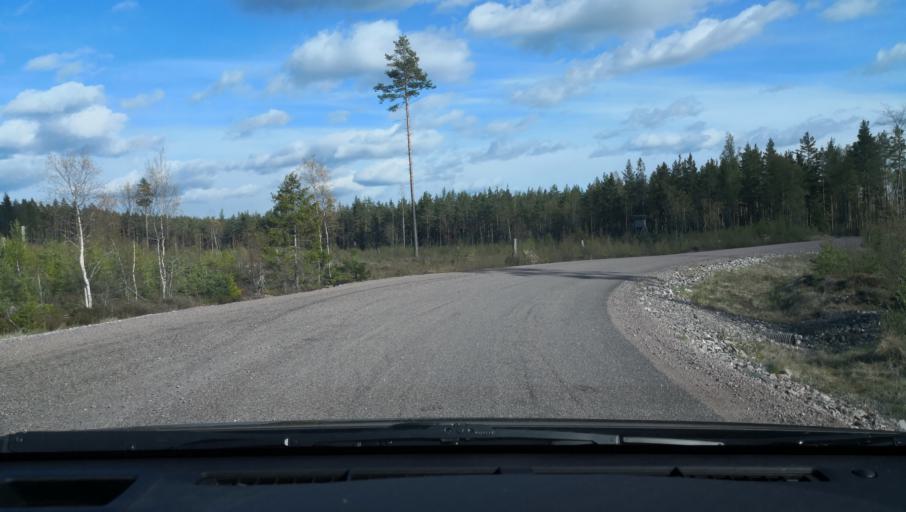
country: SE
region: OErebro
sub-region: Askersunds Kommun
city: Asbro
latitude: 58.9316
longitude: 15.0465
